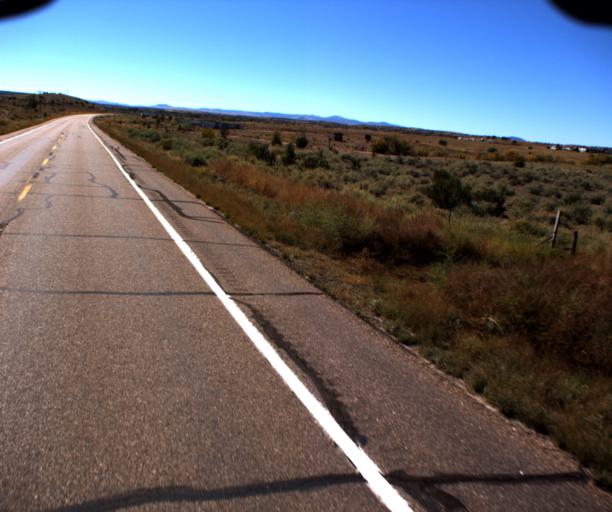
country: US
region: Arizona
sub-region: Apache County
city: Saint Johns
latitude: 34.4297
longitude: -109.4107
